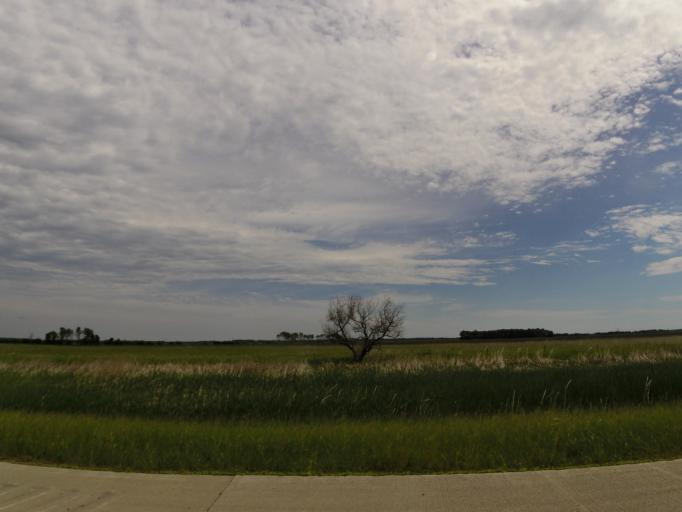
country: US
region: North Dakota
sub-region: Grand Forks County
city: Grand Forks
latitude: 48.0441
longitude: -97.1460
